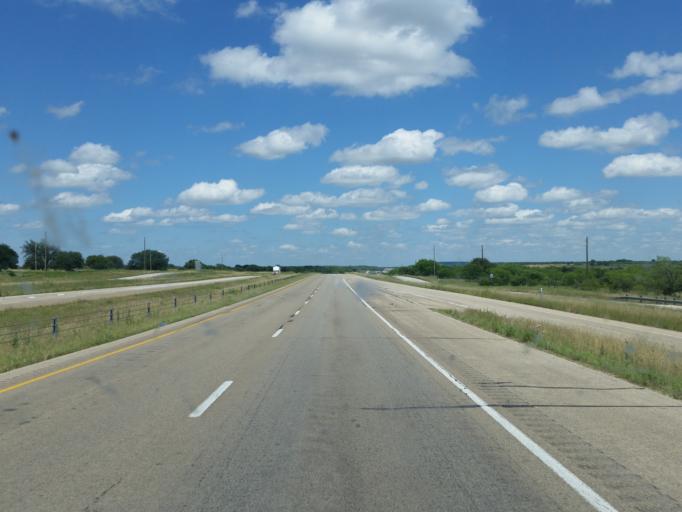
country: US
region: Texas
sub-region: Callahan County
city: Baird
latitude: 32.3855
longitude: -99.2958
